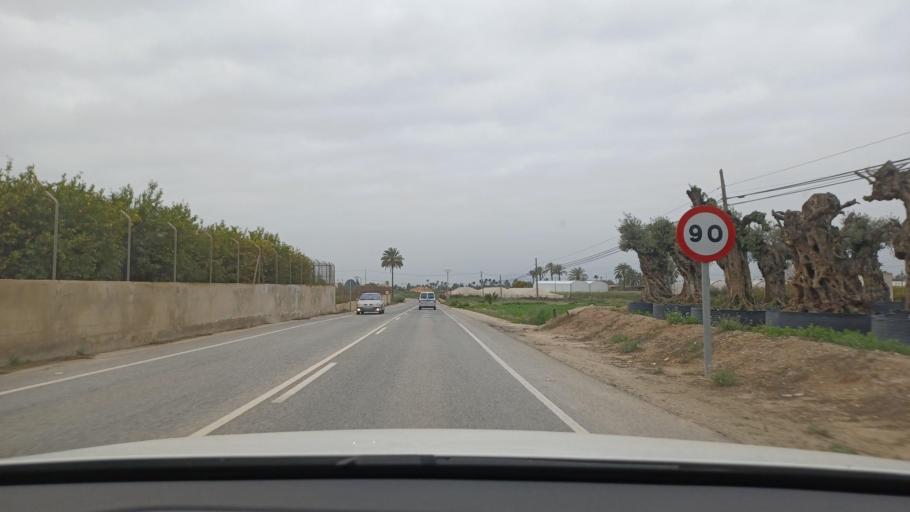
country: ES
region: Valencia
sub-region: Provincia de Alicante
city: Elche
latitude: 38.2384
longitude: -0.7119
